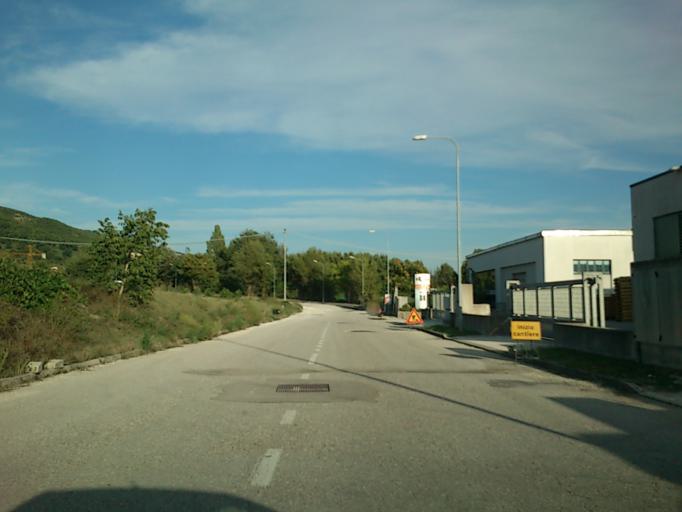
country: IT
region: The Marches
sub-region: Provincia di Pesaro e Urbino
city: Canavaccio
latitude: 43.6903
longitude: 12.7045
